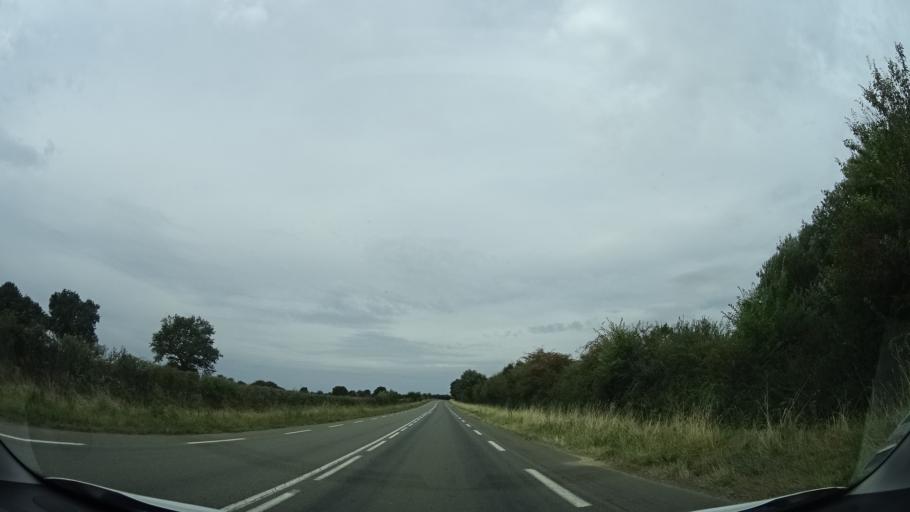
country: FR
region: Pays de la Loire
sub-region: Departement de la Sarthe
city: Auvers-le-Hamon
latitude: 47.8815
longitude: -0.4038
